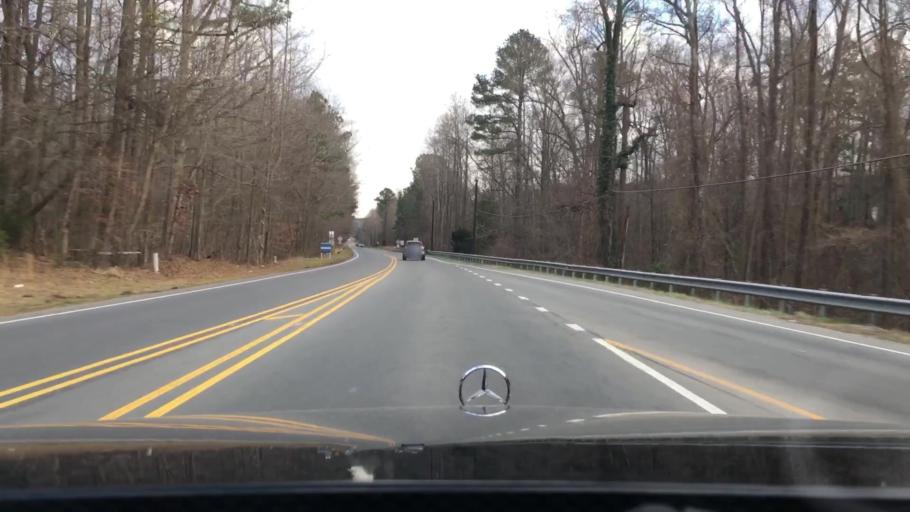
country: US
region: North Carolina
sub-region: Orange County
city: Hillsborough
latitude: 36.0558
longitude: -79.0485
